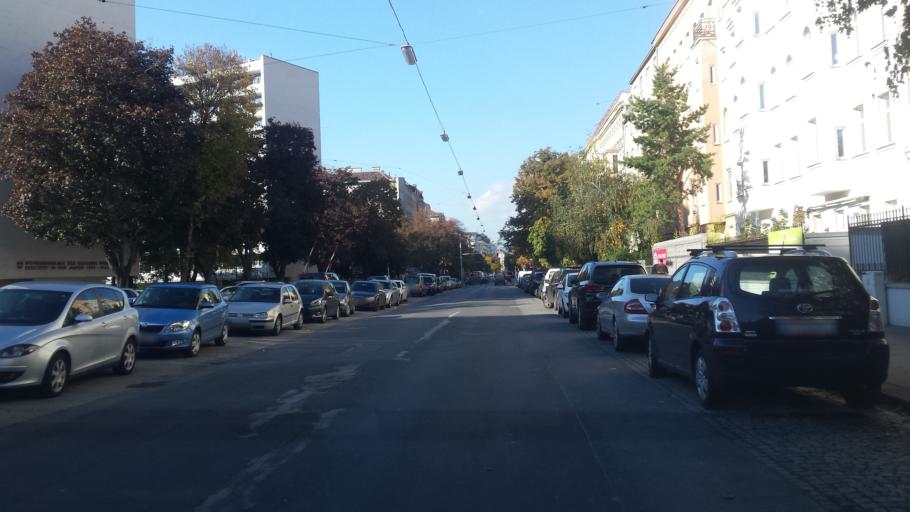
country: AT
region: Vienna
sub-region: Wien Stadt
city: Vienna
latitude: 48.2218
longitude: 16.4050
